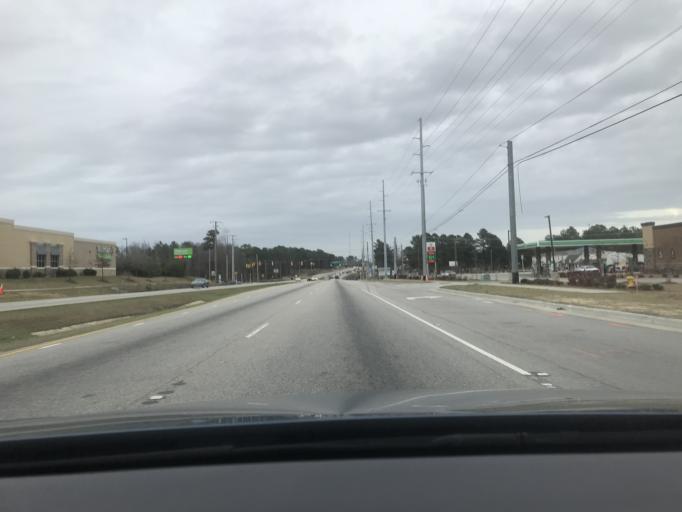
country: US
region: North Carolina
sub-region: Hoke County
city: Rockfish
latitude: 35.0395
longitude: -78.9992
